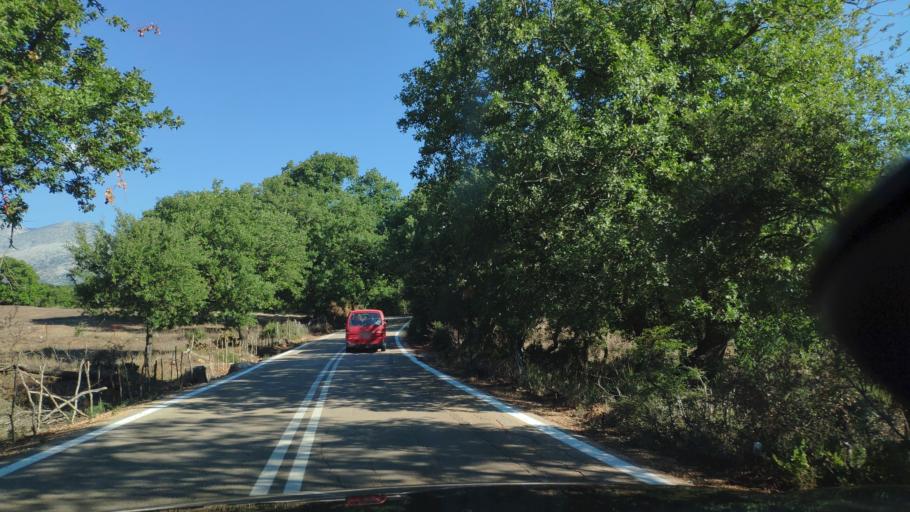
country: GR
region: West Greece
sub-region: Nomos Aitolias kai Akarnanias
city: Fitiai
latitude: 38.6896
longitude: 21.1144
